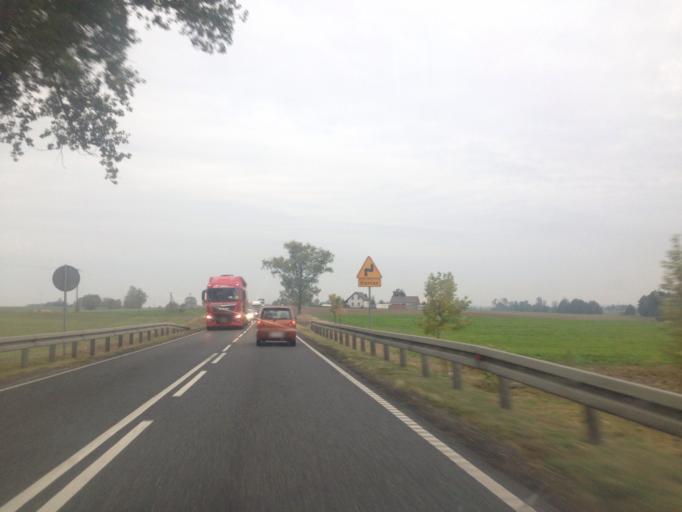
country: PL
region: Kujawsko-Pomorskie
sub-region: Powiat mogilenski
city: Mogilno
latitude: 52.6196
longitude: 17.9664
